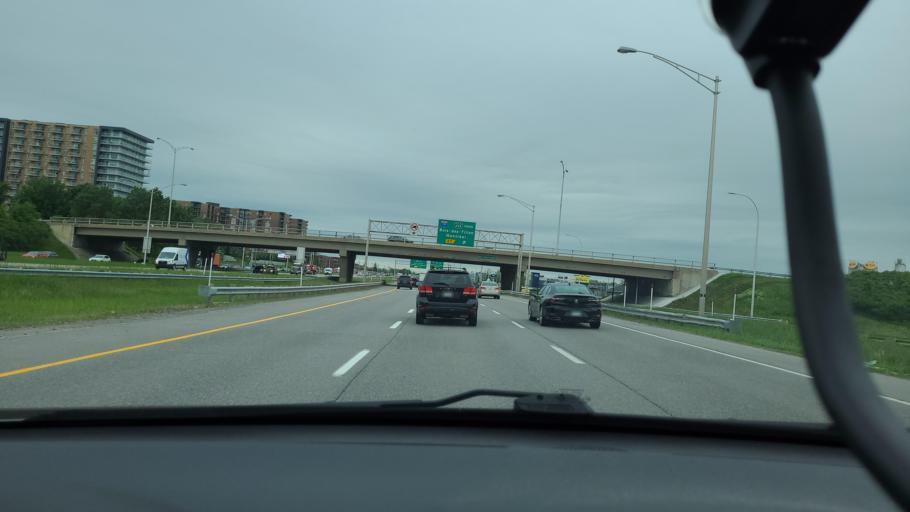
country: CA
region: Quebec
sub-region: Laval
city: Laval
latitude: 45.5969
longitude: -73.7086
